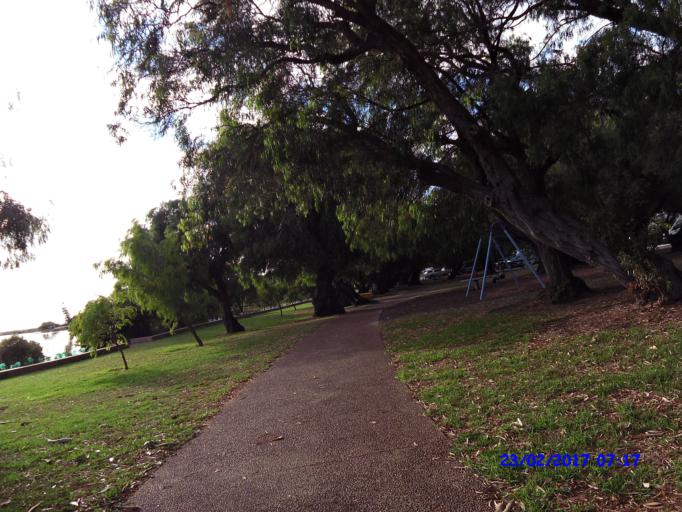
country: AU
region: Western Australia
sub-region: Augusta-Margaret River Shire
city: Augusta
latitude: -34.3235
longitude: 115.1649
